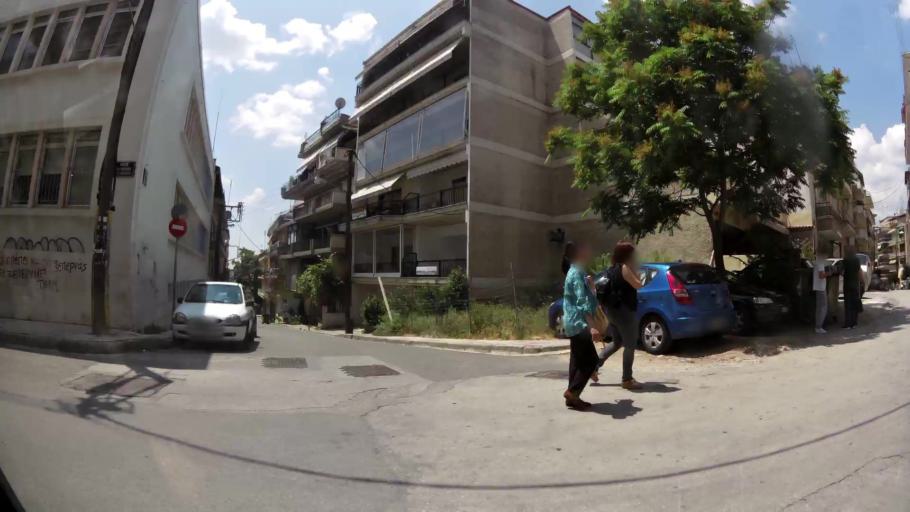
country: GR
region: West Macedonia
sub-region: Nomos Kozanis
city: Kozani
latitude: 40.2994
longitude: 21.7925
